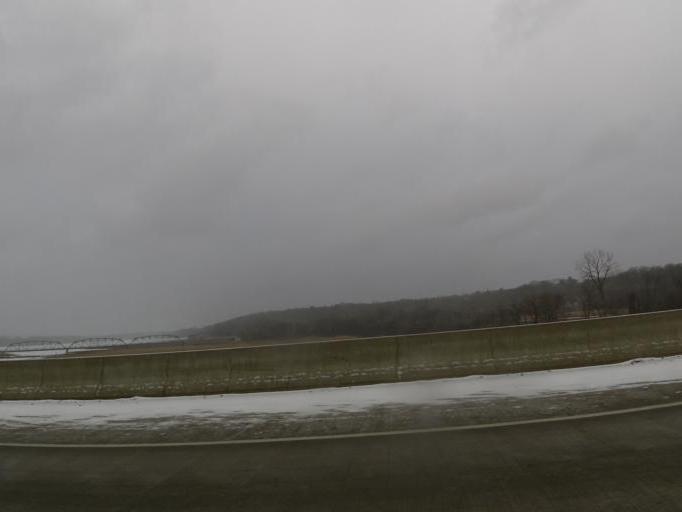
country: US
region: Minnesota
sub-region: Hennepin County
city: Bloomington
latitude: 44.8341
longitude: -93.2390
